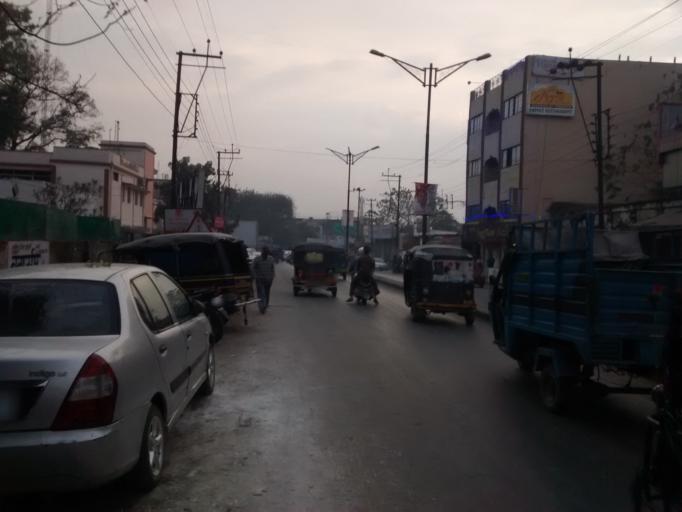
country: IN
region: Uttarakhand
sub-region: Dehradun
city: Dehradun
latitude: 30.3187
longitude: 78.0400
